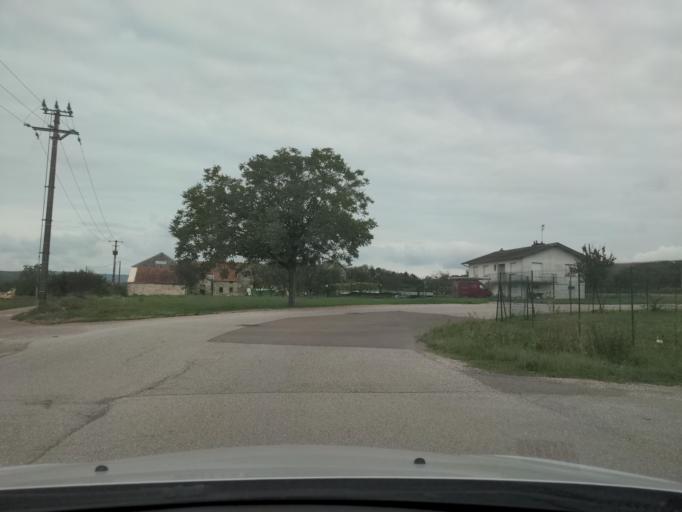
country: FR
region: Bourgogne
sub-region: Departement de la Cote-d'Or
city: Ahuy
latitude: 47.3646
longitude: 5.0375
